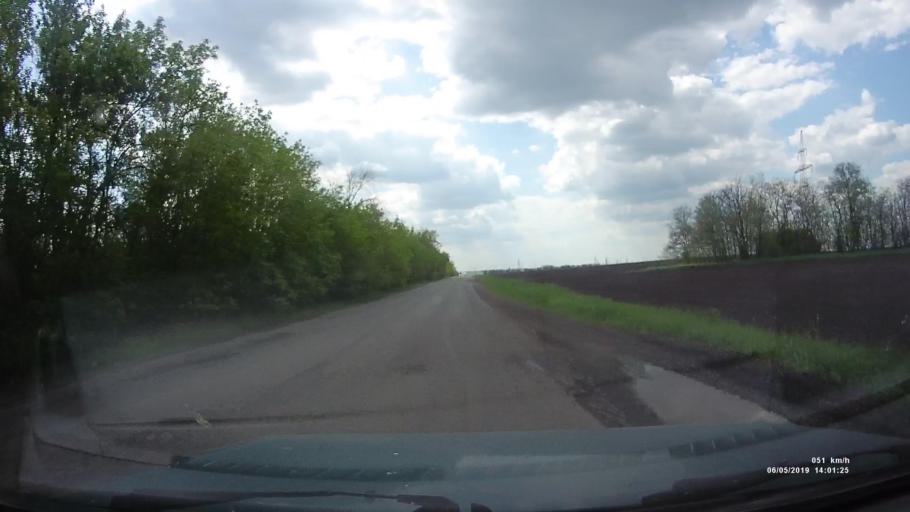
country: RU
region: Rostov
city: Shakhty
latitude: 47.6847
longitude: 40.3784
